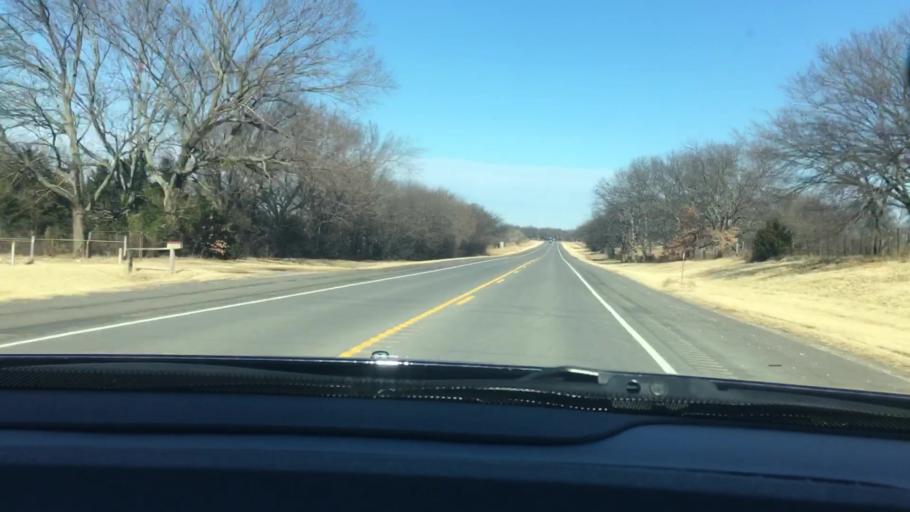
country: US
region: Oklahoma
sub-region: Murray County
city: Davis
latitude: 34.5211
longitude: -97.1205
